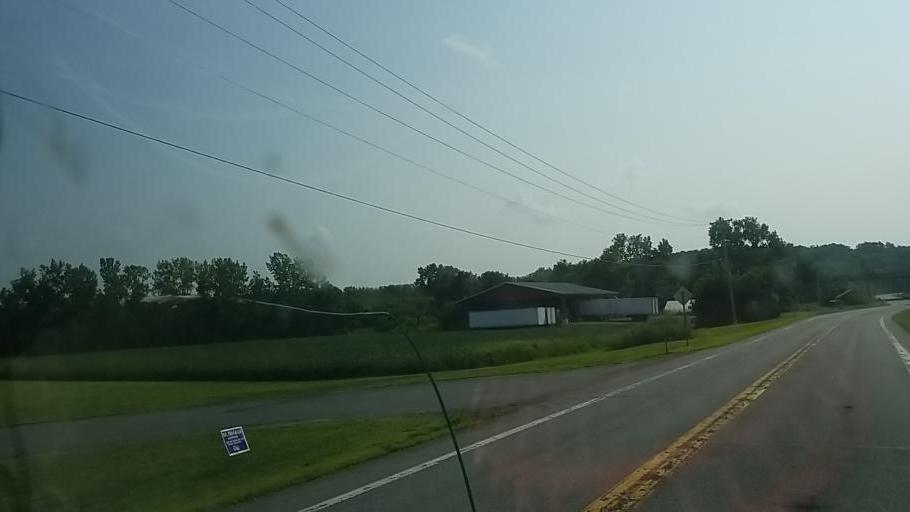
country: US
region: New York
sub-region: Montgomery County
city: Tribes Hill
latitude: 42.9331
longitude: -74.2857
